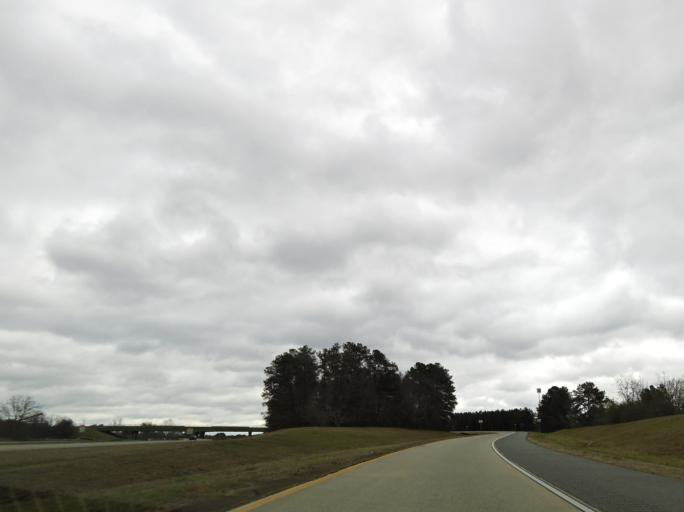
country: US
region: Georgia
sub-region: Twiggs County
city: Jeffersonville
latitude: 32.6249
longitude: -83.3729
